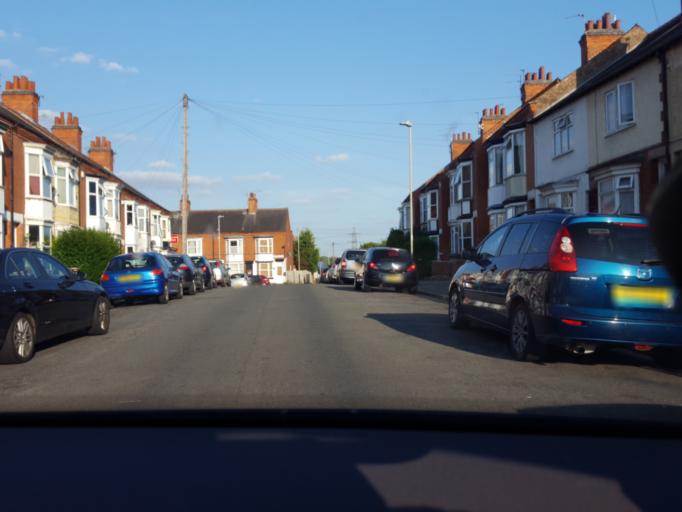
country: GB
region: England
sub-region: City of Leicester
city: Leicester
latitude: 52.6203
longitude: -1.1535
